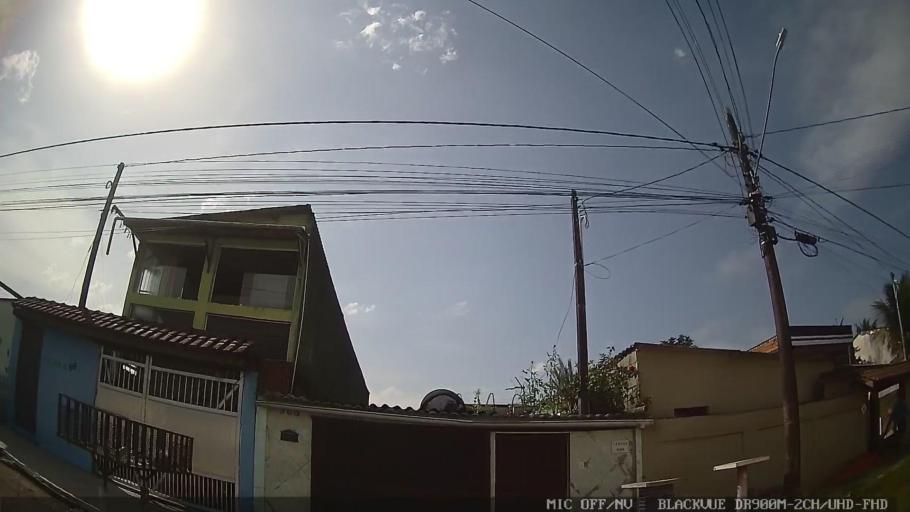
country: BR
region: Sao Paulo
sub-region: Guaruja
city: Guaruja
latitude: -23.9800
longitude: -46.2028
